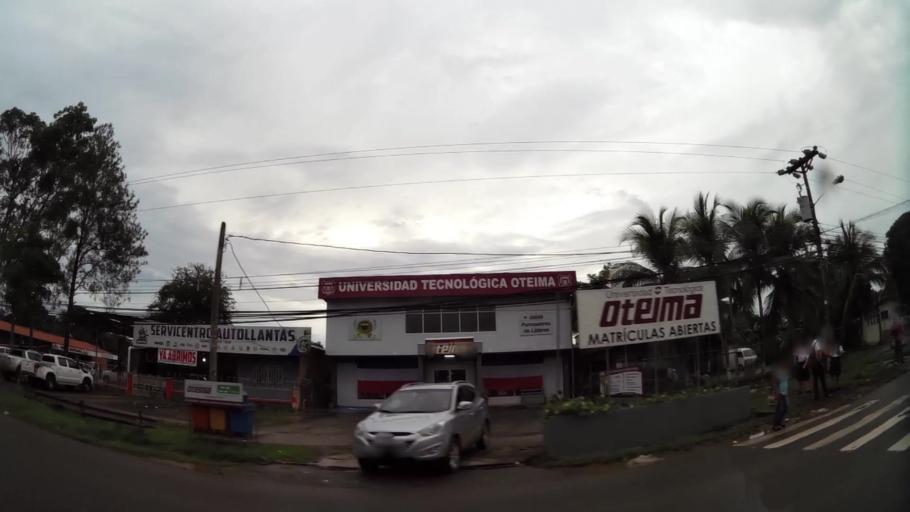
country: PA
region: Veraguas
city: Santiago de Veraguas
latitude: 8.1139
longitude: -80.9691
